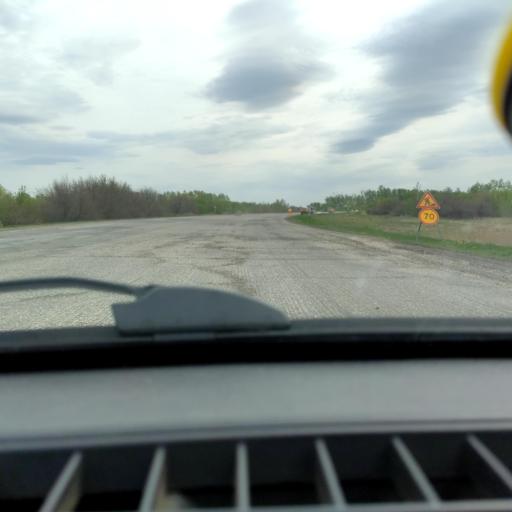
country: RU
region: Samara
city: Tol'yatti
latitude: 53.6633
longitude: 49.4227
